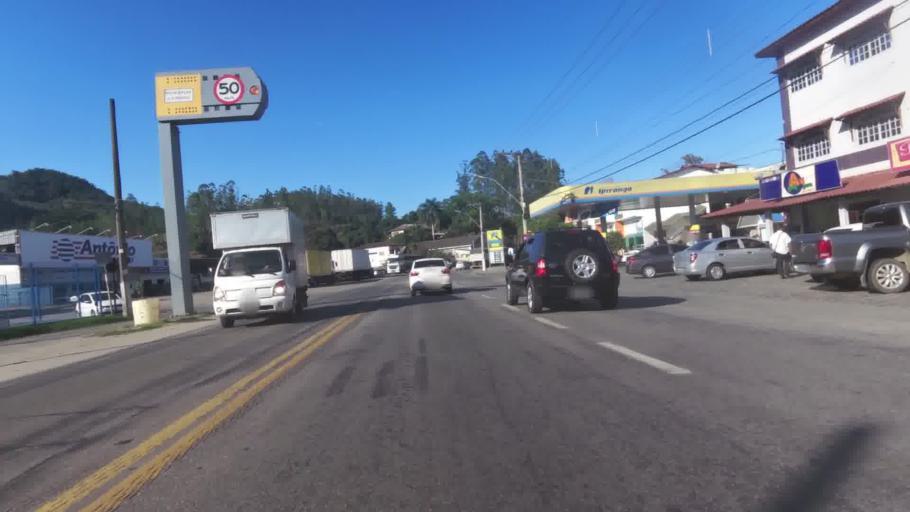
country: BR
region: Espirito Santo
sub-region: Iconha
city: Iconha
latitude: -20.7930
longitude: -40.8089
